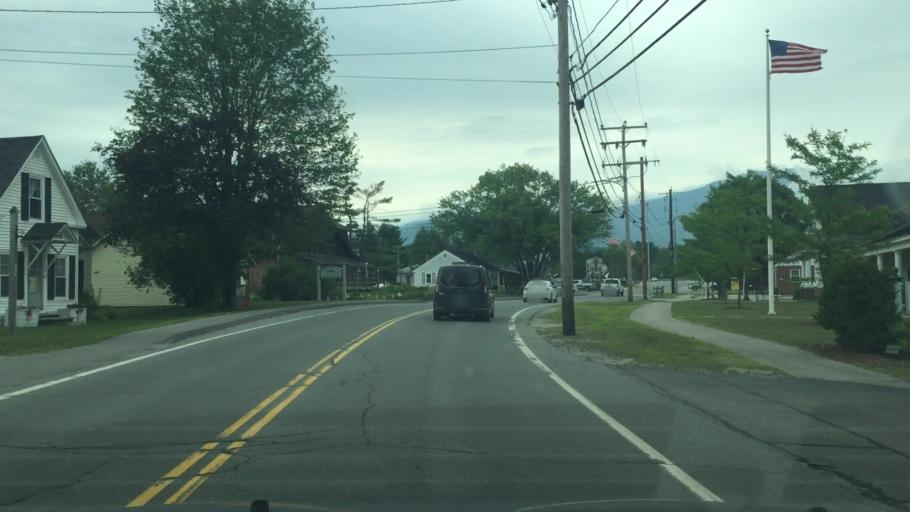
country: US
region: New Hampshire
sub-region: Grafton County
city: Littleton
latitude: 44.2287
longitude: -71.7507
